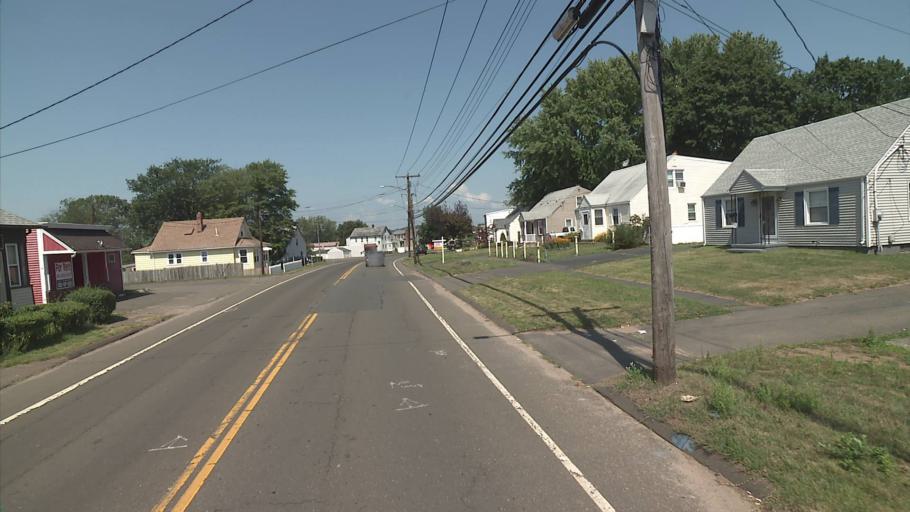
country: US
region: Connecticut
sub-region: New Haven County
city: East Haven
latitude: 41.2634
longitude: -72.8683
